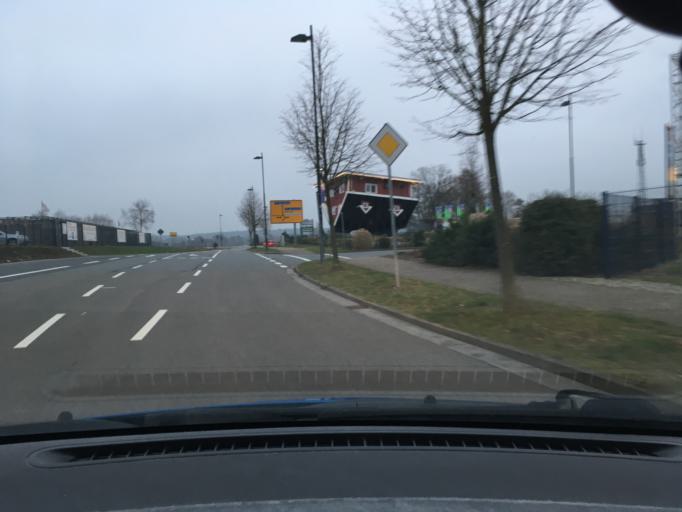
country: DE
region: Lower Saxony
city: Bispingen
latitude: 53.1001
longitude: 9.9803
